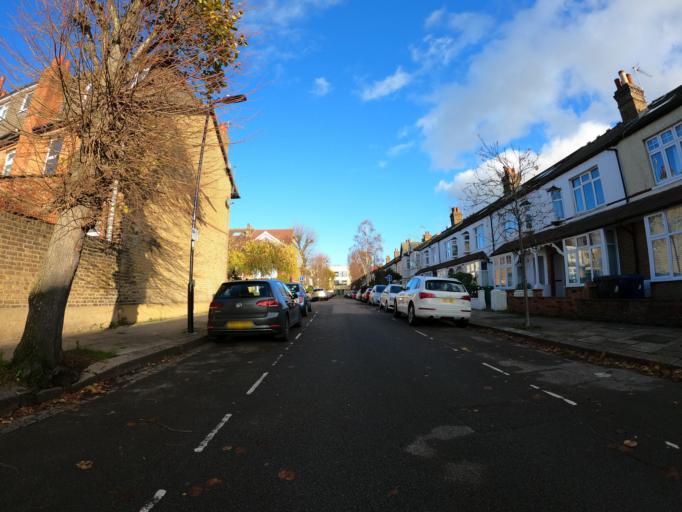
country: GB
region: England
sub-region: Greater London
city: Brentford
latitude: 51.4951
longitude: -0.3138
